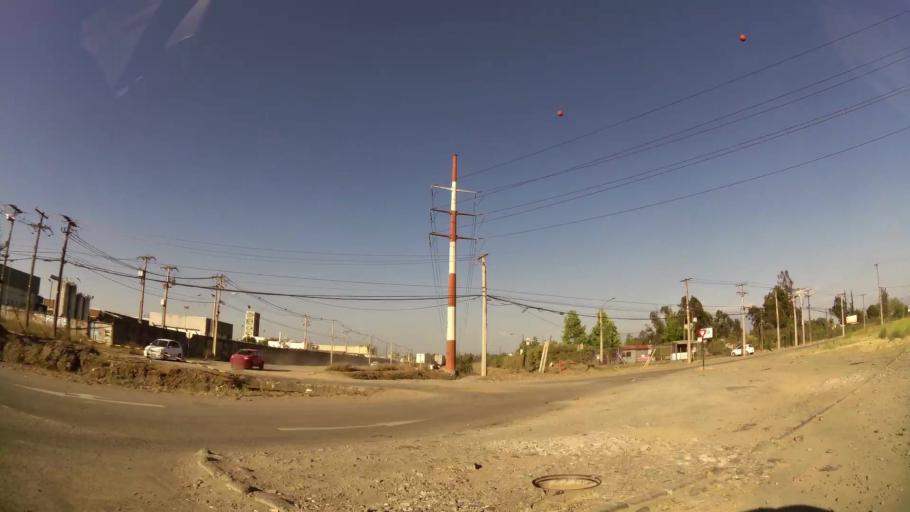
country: CL
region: Santiago Metropolitan
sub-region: Provincia de Maipo
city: San Bernardo
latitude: -33.5403
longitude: -70.7648
